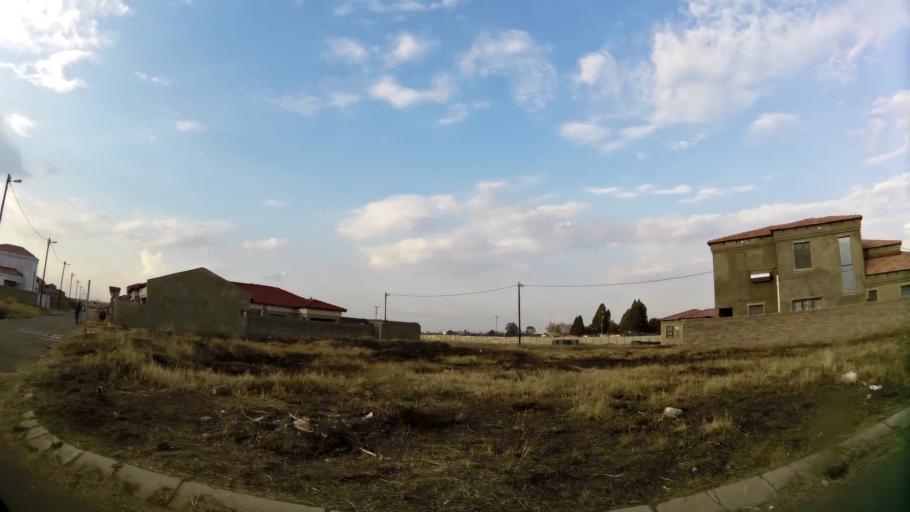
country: ZA
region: Gauteng
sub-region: Sedibeng District Municipality
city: Vanderbijlpark
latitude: -26.6101
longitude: 27.8142
